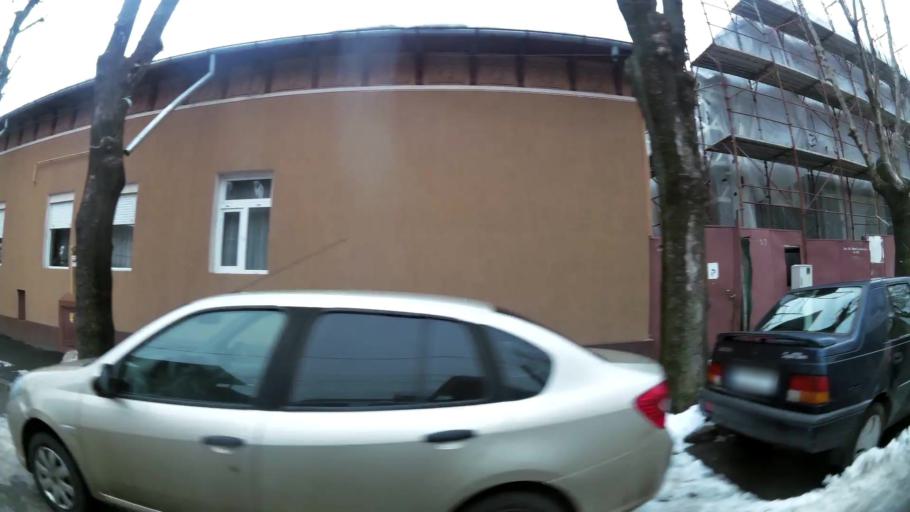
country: RO
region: Bucuresti
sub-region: Municipiul Bucuresti
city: Bucharest
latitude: 44.4291
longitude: 26.1287
